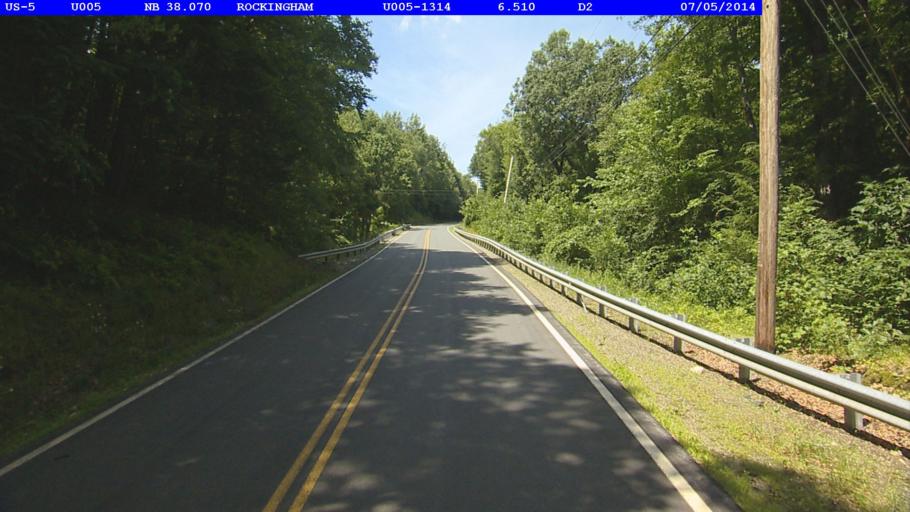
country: US
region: New Hampshire
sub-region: Sullivan County
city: Charlestown
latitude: 43.2086
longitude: -72.4496
